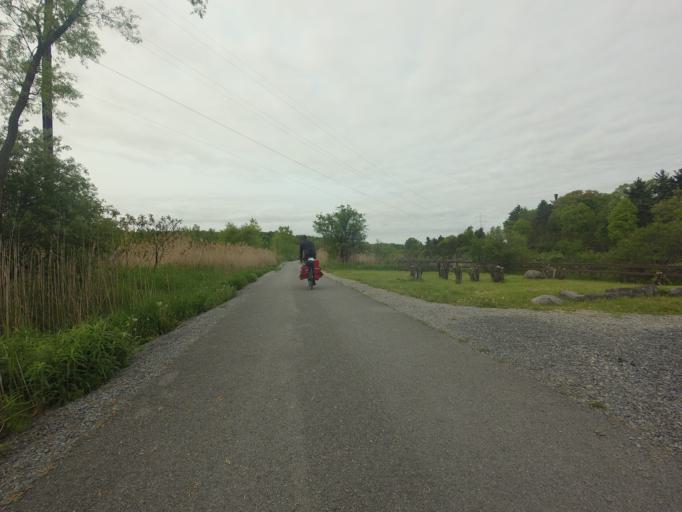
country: US
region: New York
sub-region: Jefferson County
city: Black River
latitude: 44.0023
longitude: -75.8053
